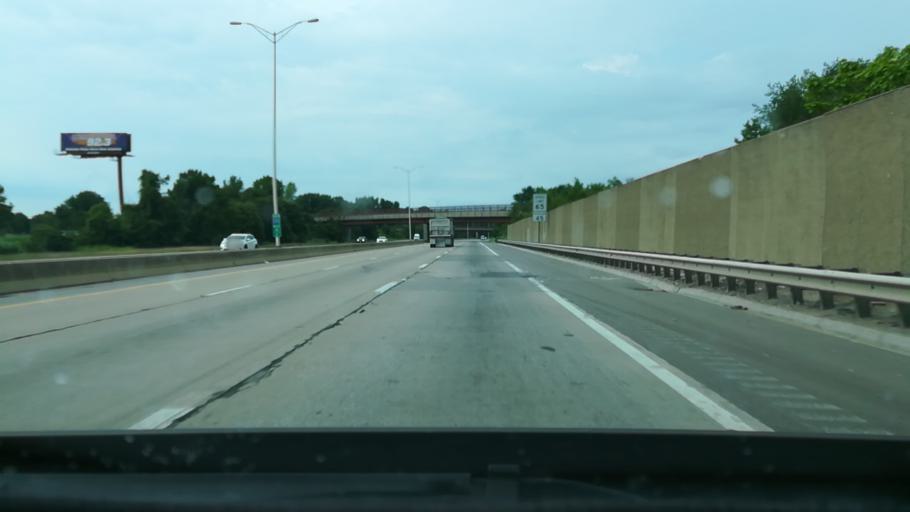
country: US
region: Illinois
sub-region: Saint Clair County
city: Alorton
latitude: 38.5974
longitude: -90.0886
